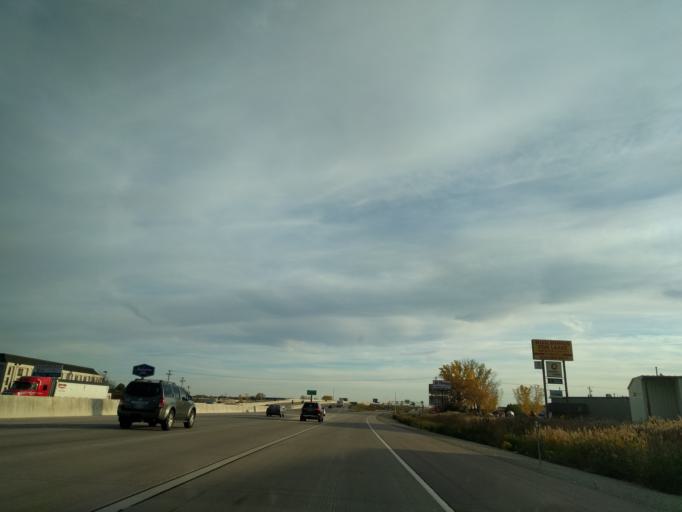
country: US
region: Wisconsin
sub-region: Brown County
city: Ashwaubenon
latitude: 44.4740
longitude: -88.0798
